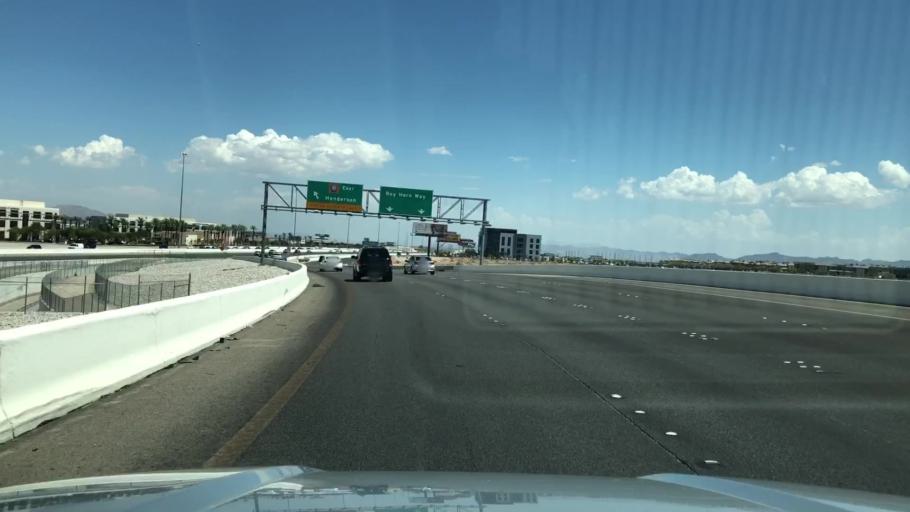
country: US
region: Nevada
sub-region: Clark County
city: Enterprise
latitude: 36.0653
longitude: -115.2784
